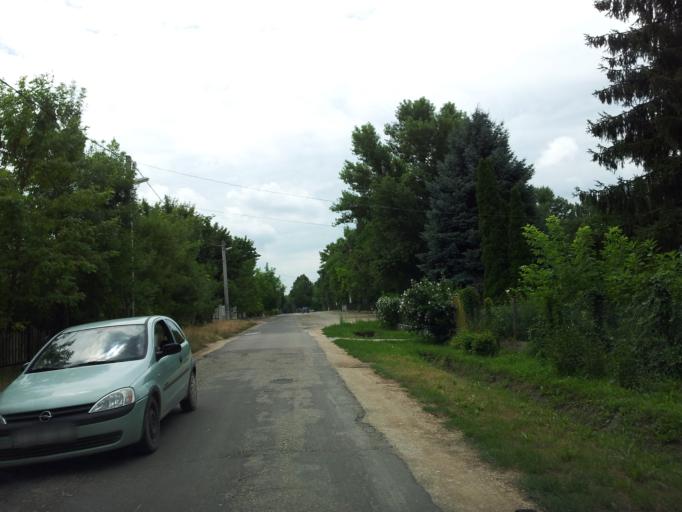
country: HU
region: Pest
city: Rackeve
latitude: 47.1976
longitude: 18.9595
